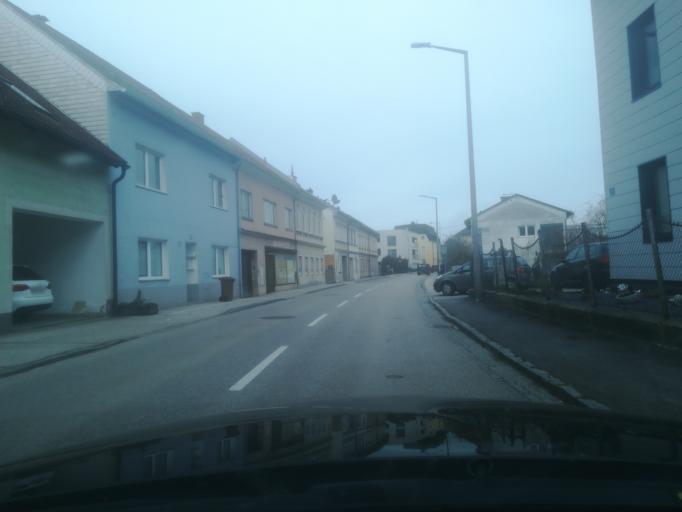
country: AT
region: Upper Austria
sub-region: Wels-Land
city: Thalheim bei Wels
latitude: 48.1517
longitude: 14.0247
